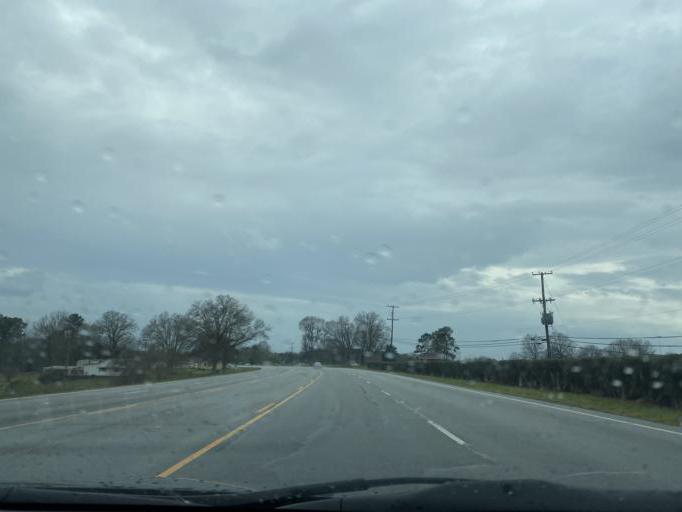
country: US
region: South Carolina
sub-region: Cherokee County
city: Gaffney
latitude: 35.0508
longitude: -81.6931
